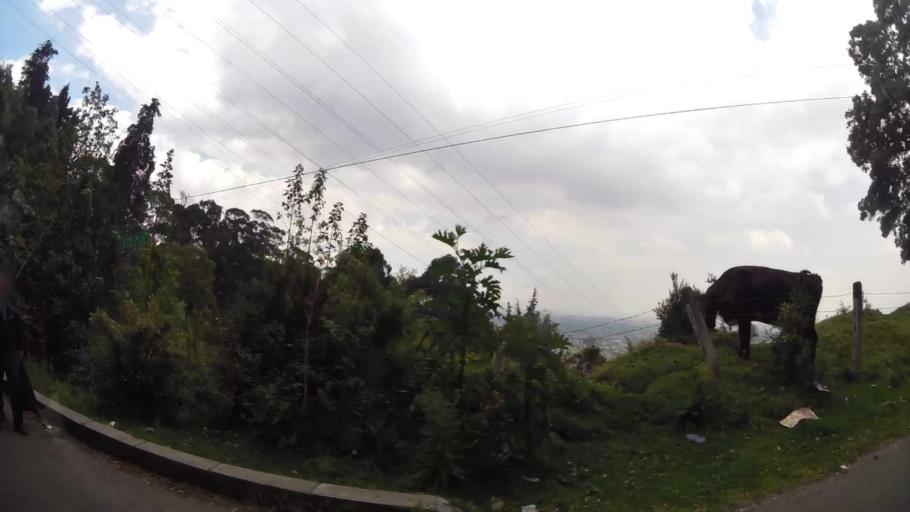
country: CO
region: Bogota D.C.
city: Bogota
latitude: 4.5941
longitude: -74.0652
